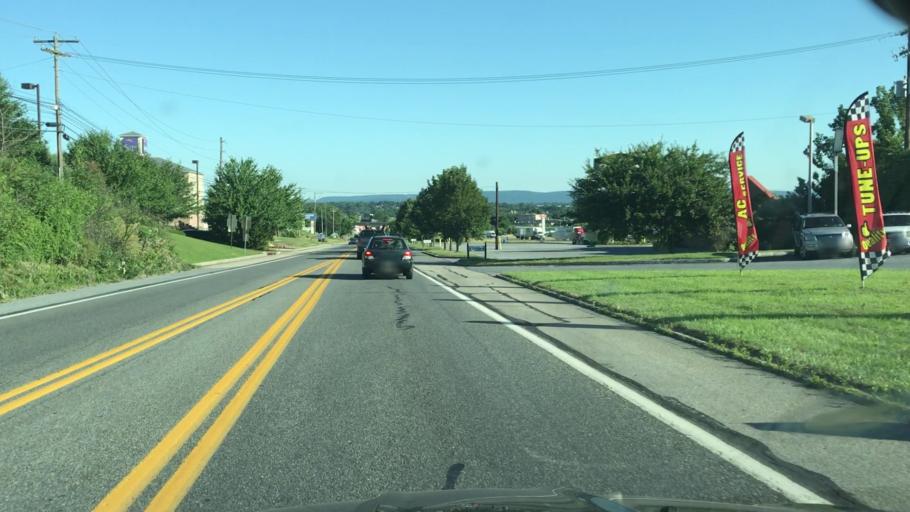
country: US
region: Pennsylvania
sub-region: Dauphin County
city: Lawnton
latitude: 40.2434
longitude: -76.8081
